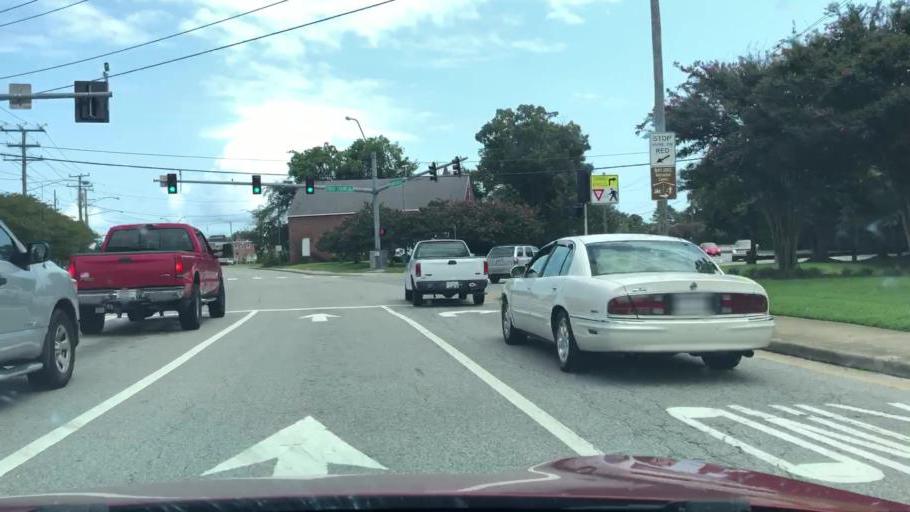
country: US
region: Virginia
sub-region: City of Norfolk
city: Norfolk
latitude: 36.8973
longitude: -76.1384
